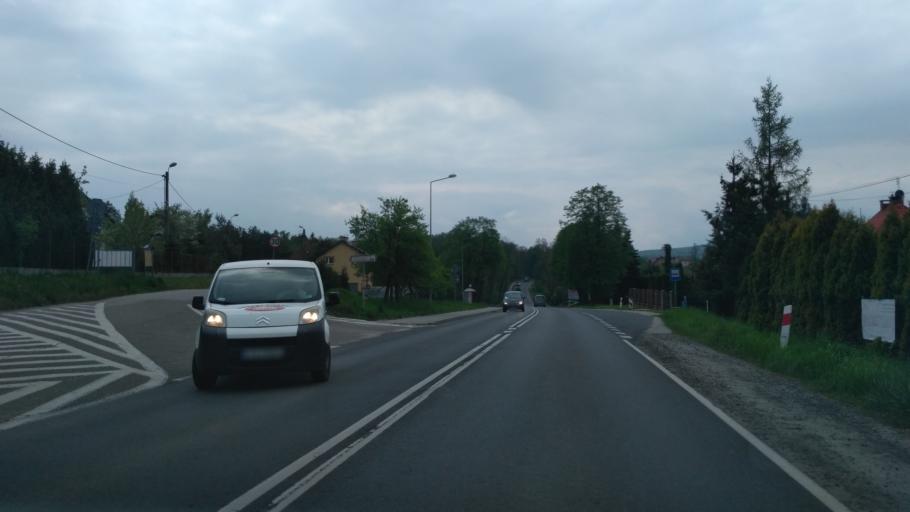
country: PL
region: Lesser Poland Voivodeship
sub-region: Powiat tarnowski
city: Tarnowiec
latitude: 49.9773
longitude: 20.9885
